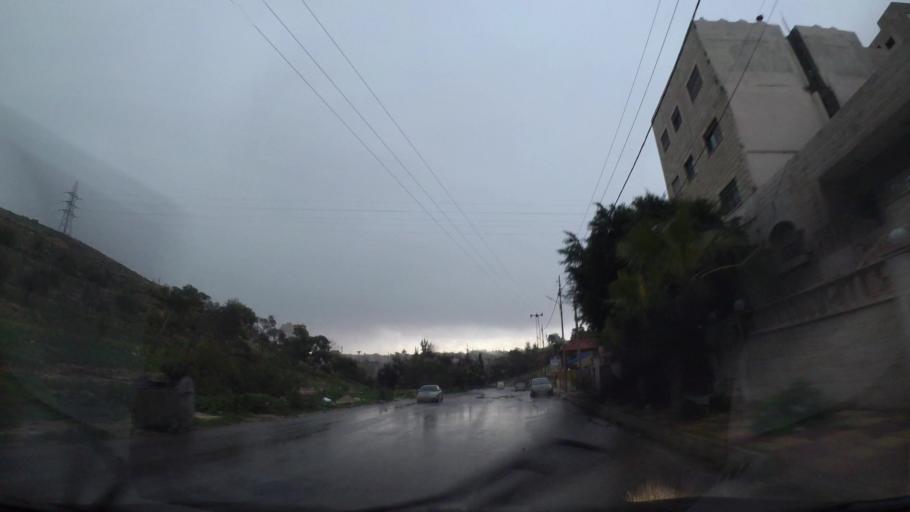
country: JO
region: Amman
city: Amman
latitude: 31.9924
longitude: 35.9736
